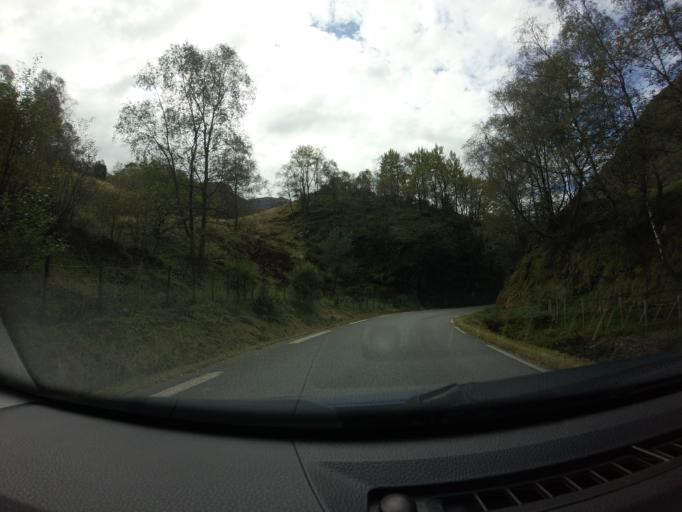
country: NO
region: Rogaland
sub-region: Forsand
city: Forsand
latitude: 58.8518
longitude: 6.3714
